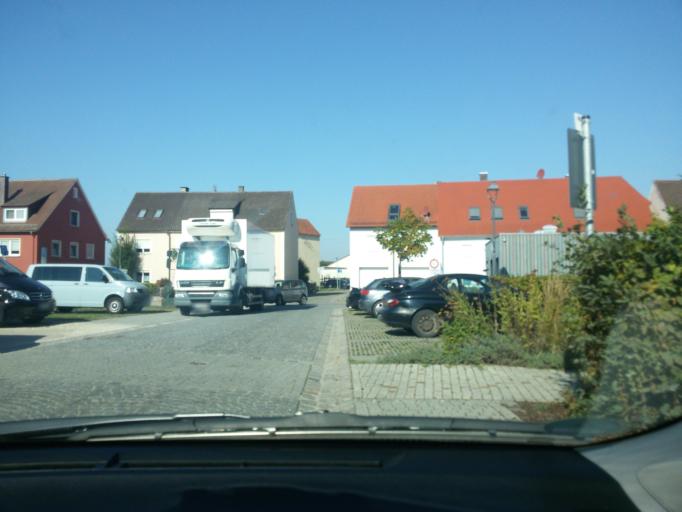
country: DE
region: Bavaria
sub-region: Regierungsbezirk Mittelfranken
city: Wassertrudingen
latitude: 49.0397
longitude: 10.5962
